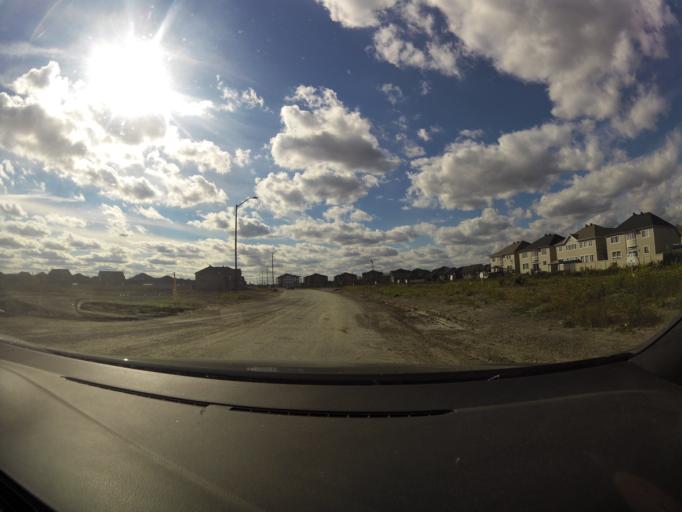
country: CA
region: Ontario
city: Bells Corners
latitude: 45.2709
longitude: -75.8857
